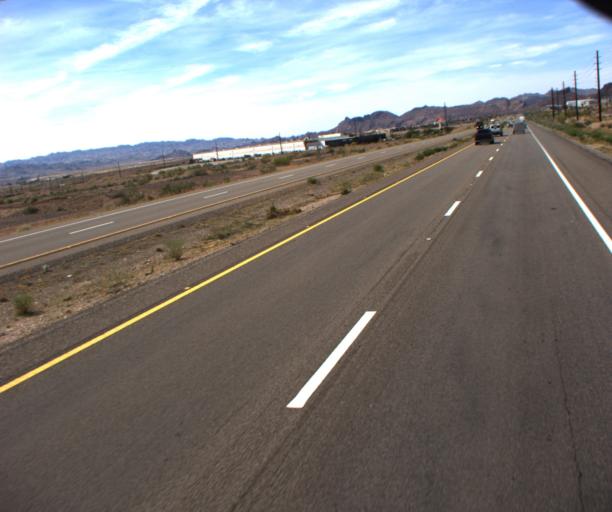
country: US
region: Arizona
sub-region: Mohave County
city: Desert Hills
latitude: 34.5572
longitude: -114.3590
